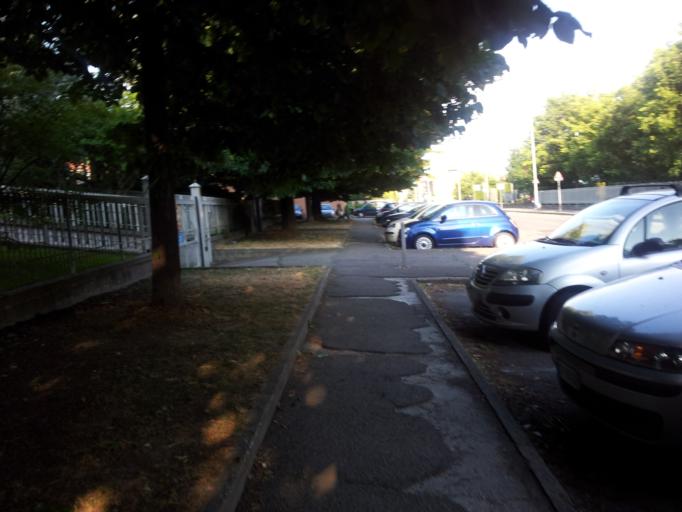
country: IT
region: Piedmont
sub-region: Provincia di Torino
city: Trofarello
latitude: 44.9807
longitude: 7.7393
